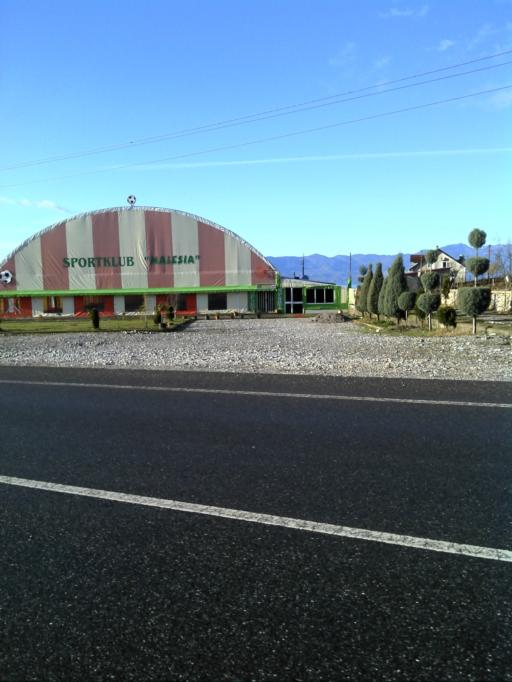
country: AL
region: Shkoder
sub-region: Rrethi i Malesia e Madhe
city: Koplik
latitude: 42.1890
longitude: 19.4568
